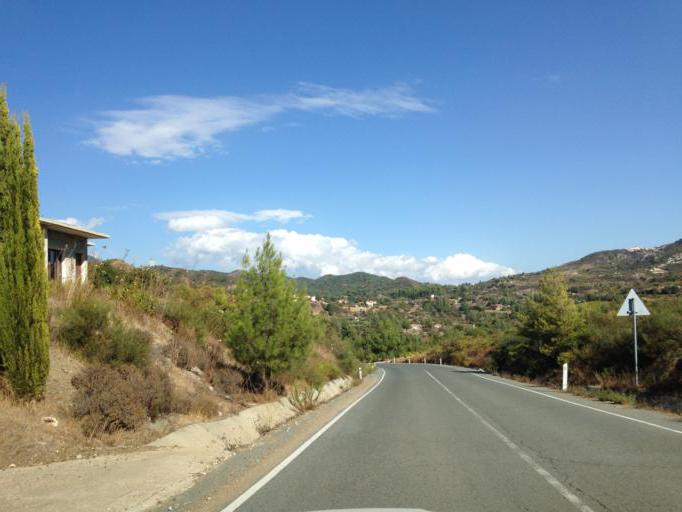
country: CY
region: Limassol
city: Pachna
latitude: 34.8672
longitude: 32.8180
